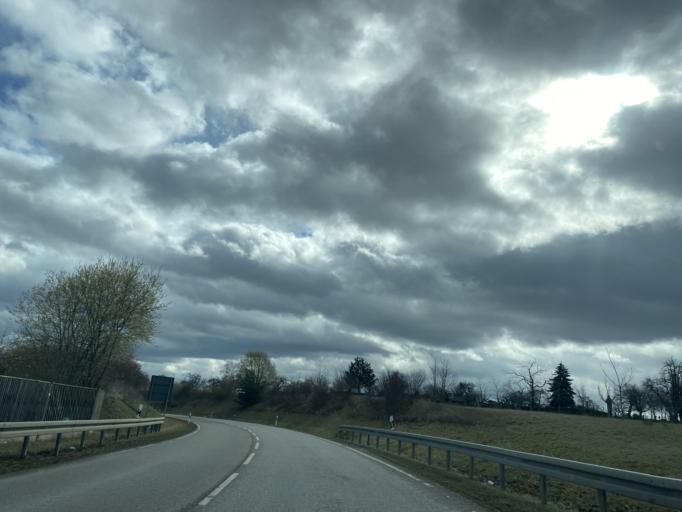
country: DE
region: Baden-Wuerttemberg
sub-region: Regierungsbezirk Stuttgart
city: Hemmingen
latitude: 48.8335
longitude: 9.0310
